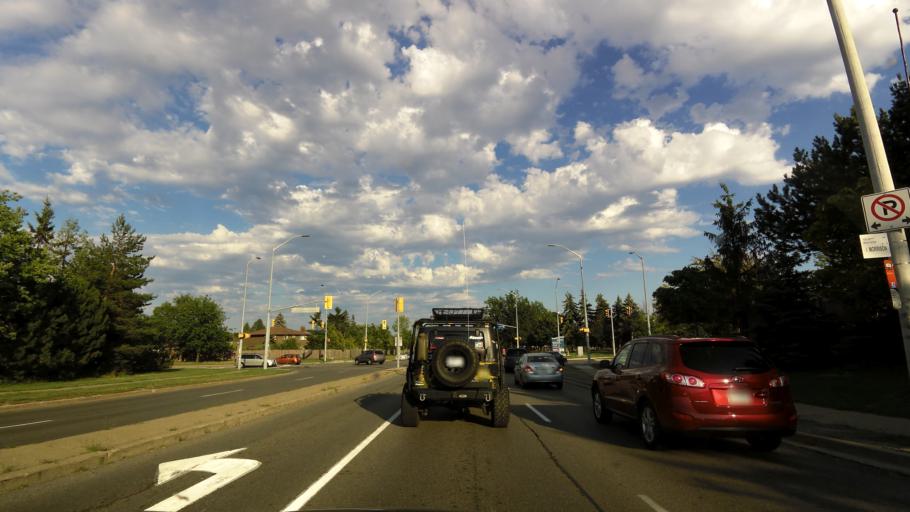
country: CA
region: Ontario
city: Mississauga
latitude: 43.5634
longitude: -79.6285
